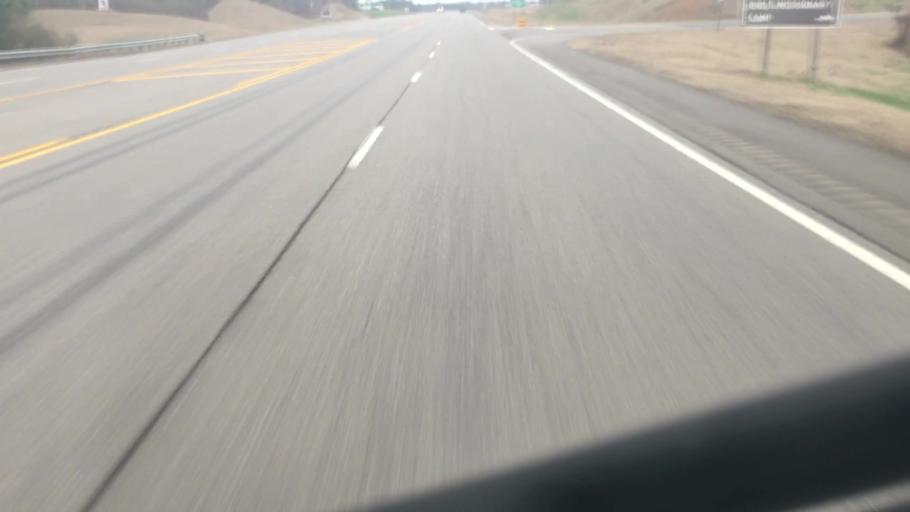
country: US
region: Alabama
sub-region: Walker County
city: Jasper
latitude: 33.8059
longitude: -87.2349
